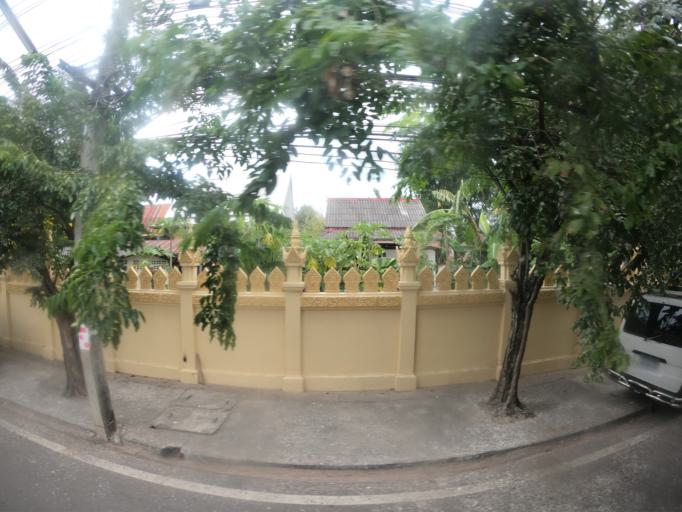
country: TH
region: Maha Sarakham
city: Maha Sarakham
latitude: 16.1797
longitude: 103.3066
